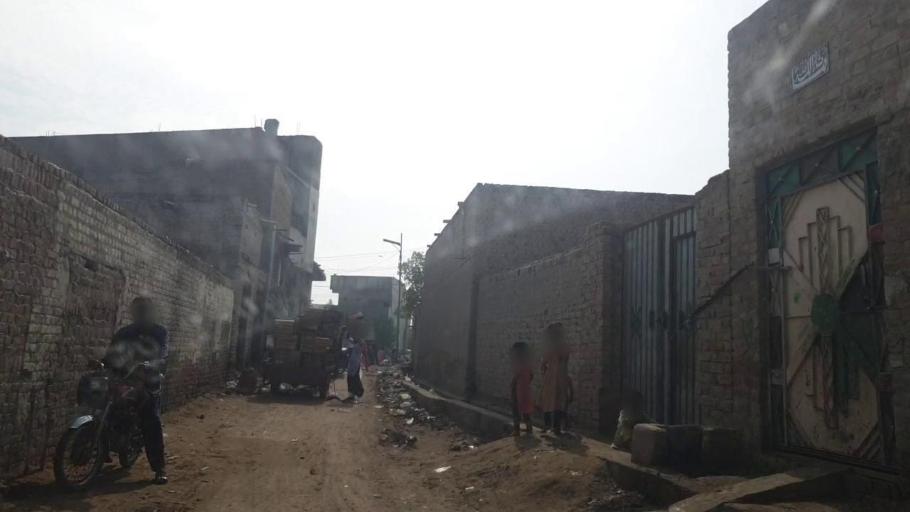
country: PK
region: Sindh
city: Khairpur
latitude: 27.5843
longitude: 68.7756
